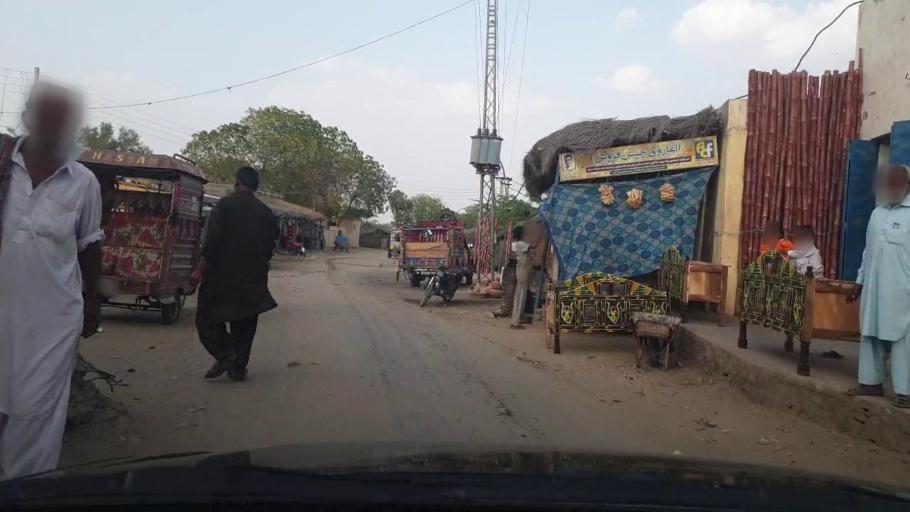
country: PK
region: Sindh
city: Islamkot
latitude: 25.0262
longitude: 70.5526
